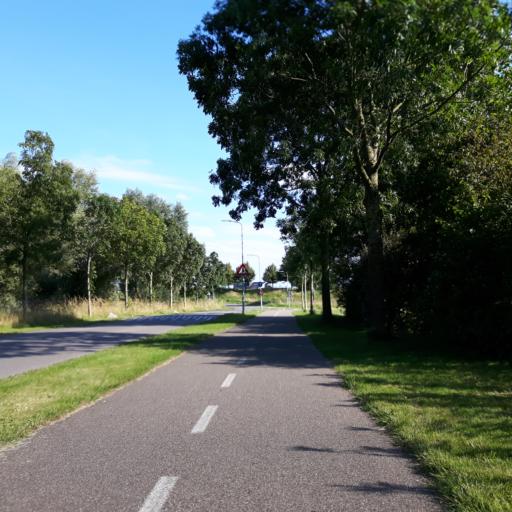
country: NL
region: Zeeland
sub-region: Gemeente Goes
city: Goes
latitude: 51.5187
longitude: 3.9127
